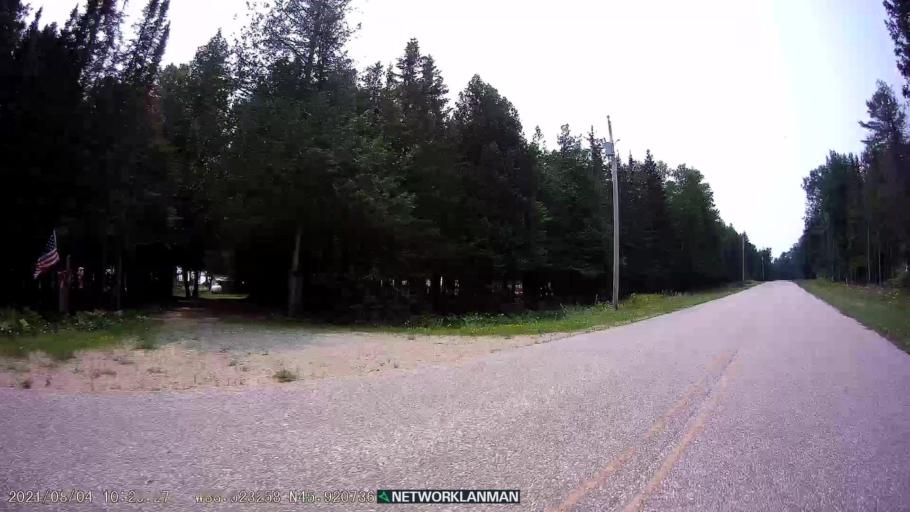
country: CA
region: Ontario
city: Thessalon
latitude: 45.9195
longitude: -83.5233
